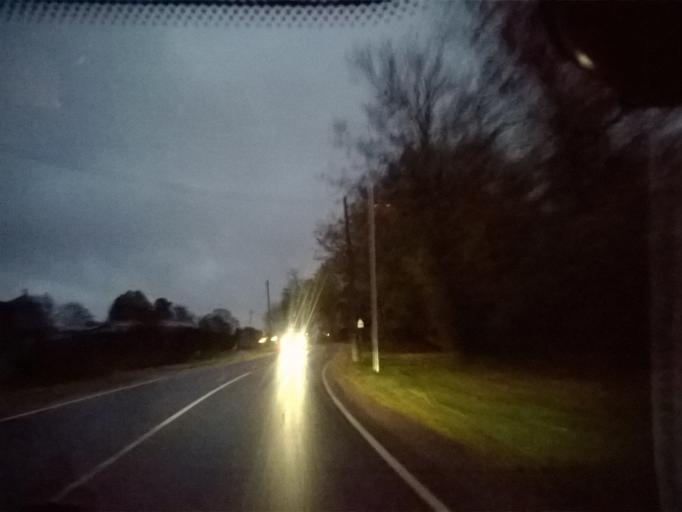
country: EE
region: Harju
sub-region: Viimsi vald
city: Viimsi
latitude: 59.5159
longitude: 24.8480
